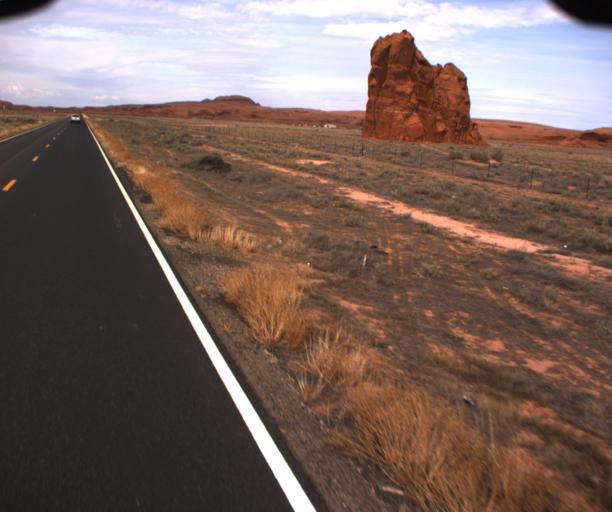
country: US
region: Arizona
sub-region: Apache County
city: Many Farms
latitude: 36.7454
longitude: -109.6399
